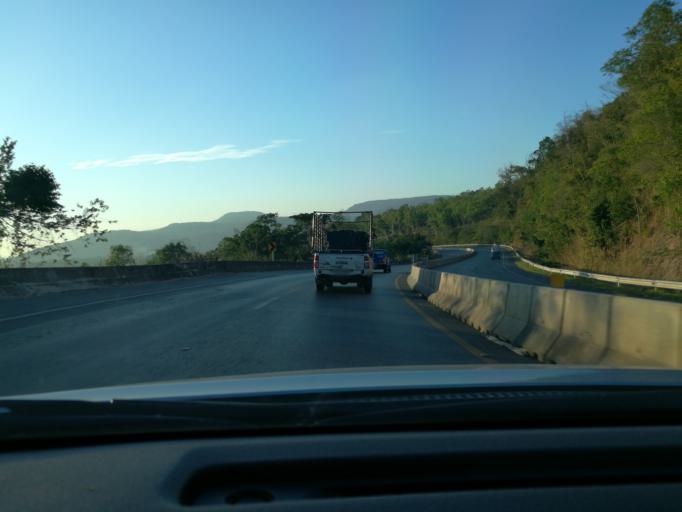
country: TH
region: Phitsanulok
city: Wang Thong
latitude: 16.8537
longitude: 100.5114
